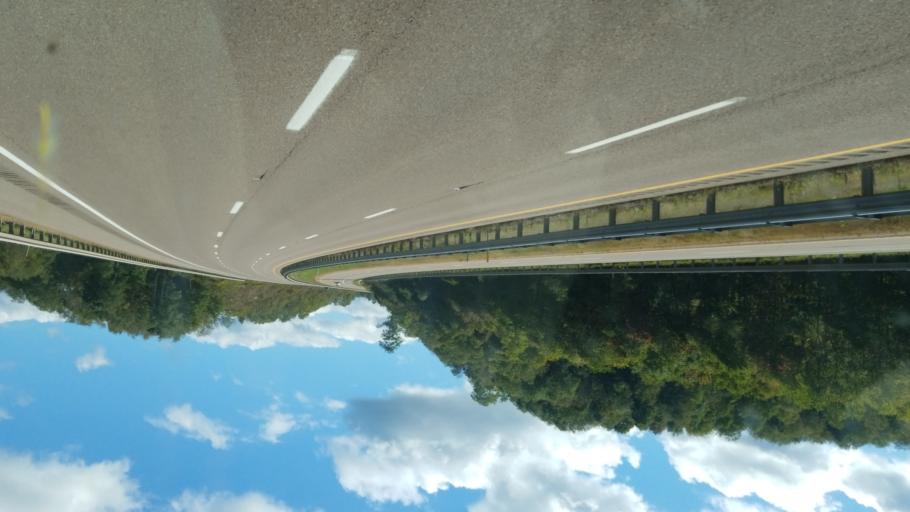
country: US
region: Pennsylvania
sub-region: Somerset County
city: Meyersdale
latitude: 39.6990
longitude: -79.2839
